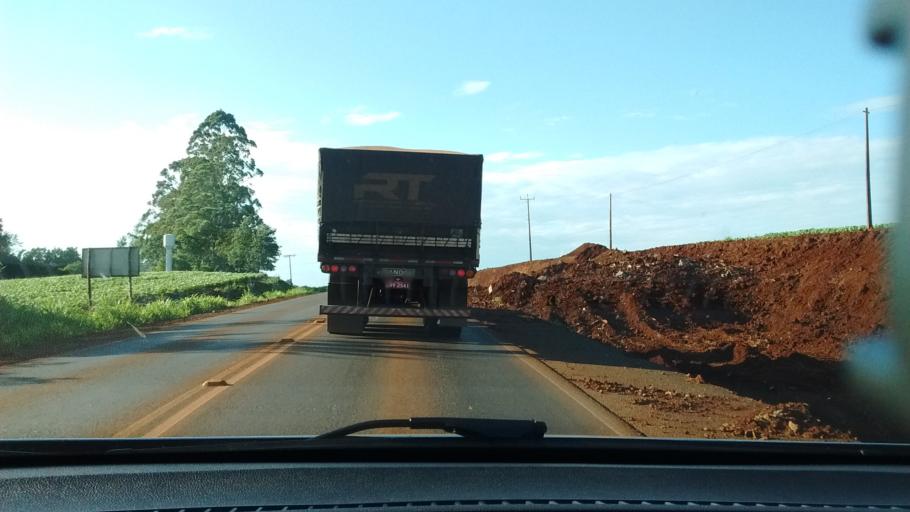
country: BR
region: Parana
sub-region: Cascavel
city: Cascavel
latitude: -25.2201
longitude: -53.5953
